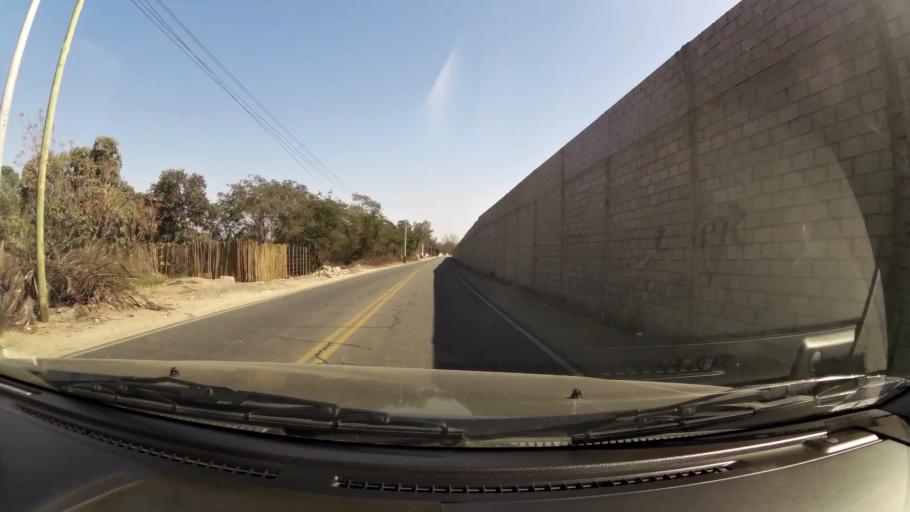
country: PE
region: Ica
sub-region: Provincia de Ica
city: San Juan Bautista
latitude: -13.9838
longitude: -75.6969
